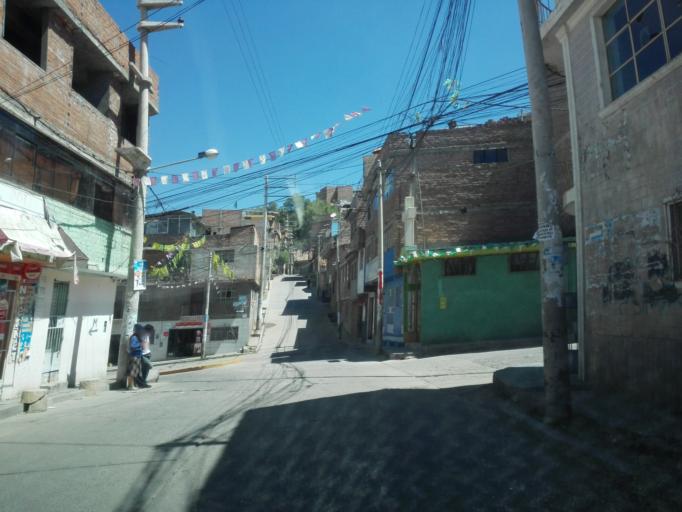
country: PE
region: Ayacucho
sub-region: Provincia de Huamanga
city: Ayacucho
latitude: -13.1583
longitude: -74.2308
